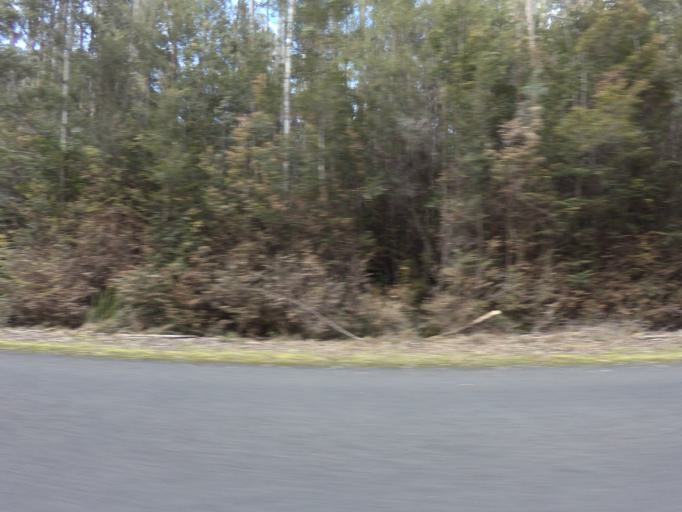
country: AU
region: Tasmania
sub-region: Huon Valley
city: Geeveston
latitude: -42.8207
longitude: 146.3009
